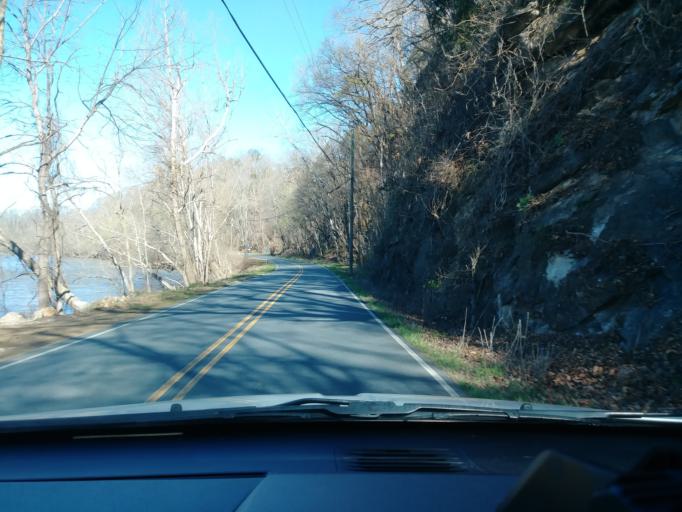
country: US
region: North Carolina
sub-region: Madison County
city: Marshall
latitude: 35.8955
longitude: -82.8229
